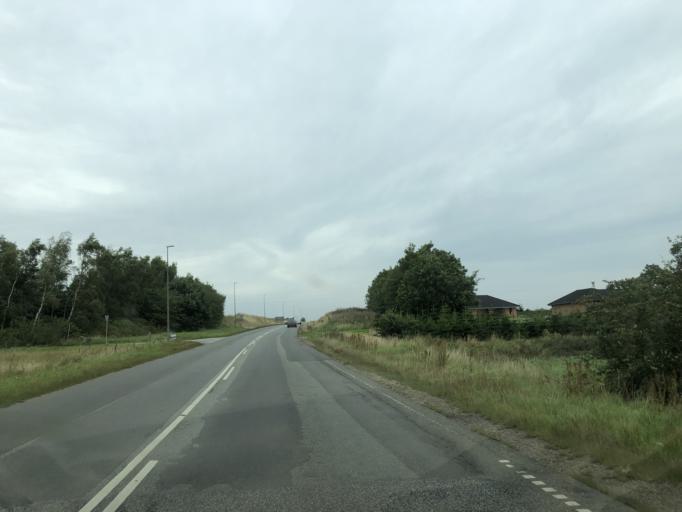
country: DK
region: North Denmark
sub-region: Morso Kommune
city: Nykobing Mors
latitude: 56.7916
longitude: 8.8343
